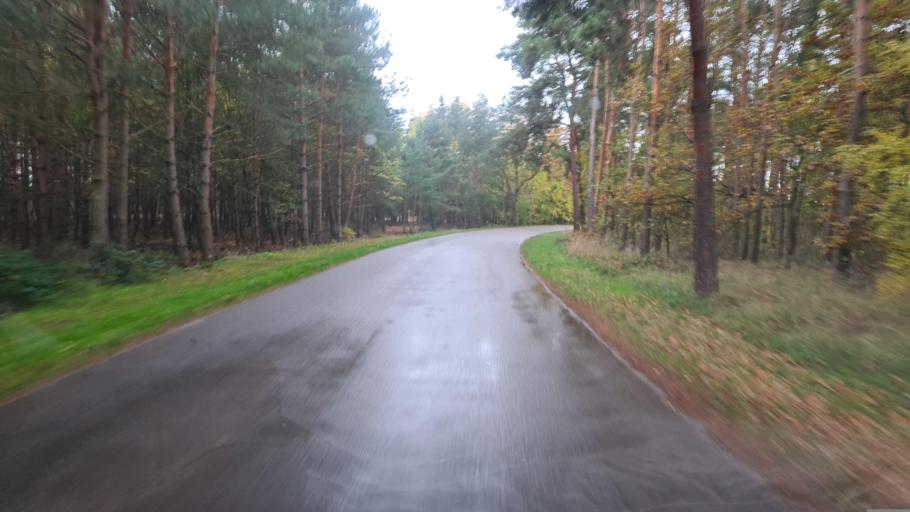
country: DE
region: Saxony-Anhalt
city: Abtsdorf
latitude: 51.9156
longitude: 12.7028
